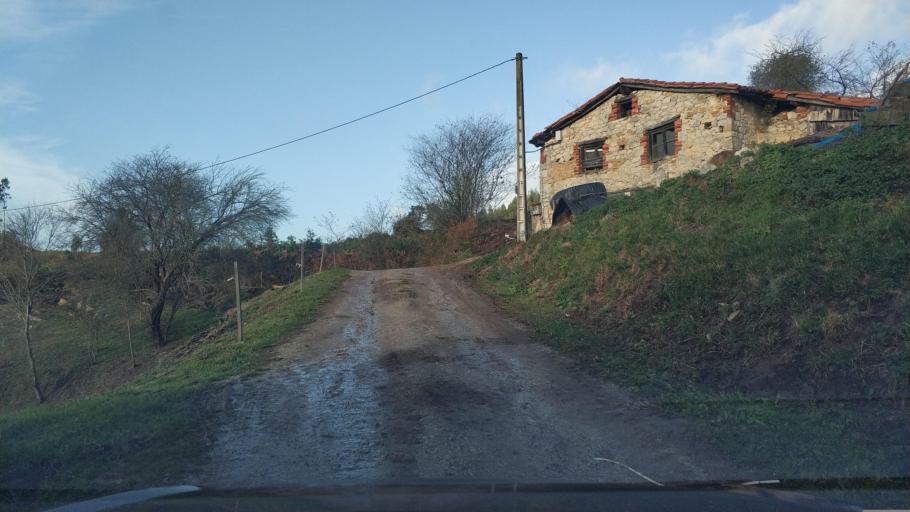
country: ES
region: Cantabria
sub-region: Provincia de Cantabria
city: Luzmela
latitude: 43.3347
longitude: -4.1982
